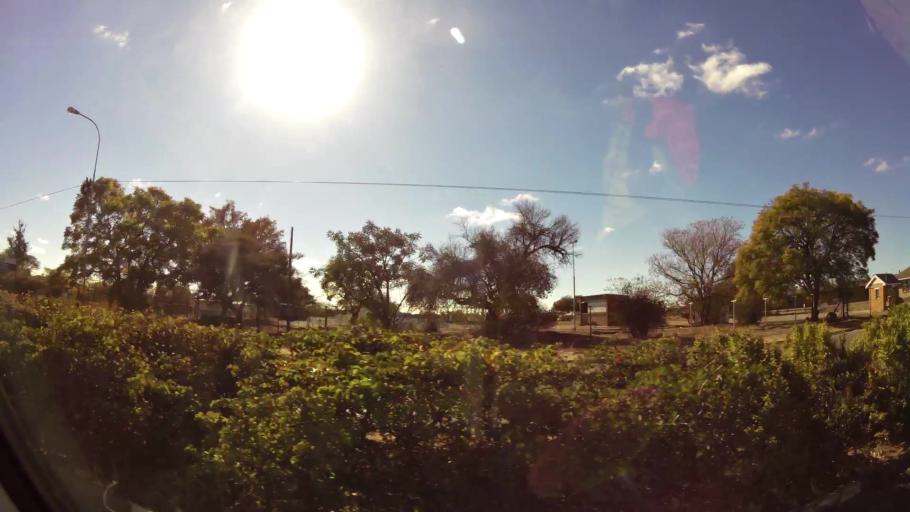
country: ZA
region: Limpopo
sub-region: Capricorn District Municipality
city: Polokwane
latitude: -23.8863
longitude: 29.4447
